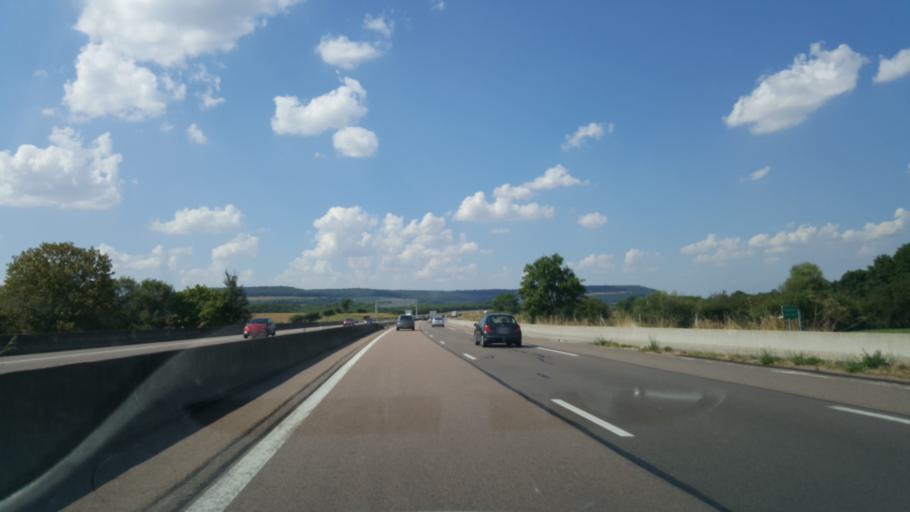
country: FR
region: Bourgogne
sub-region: Departement de la Cote-d'Or
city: Pouilly-en-Auxois
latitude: 47.2626
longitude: 4.5208
